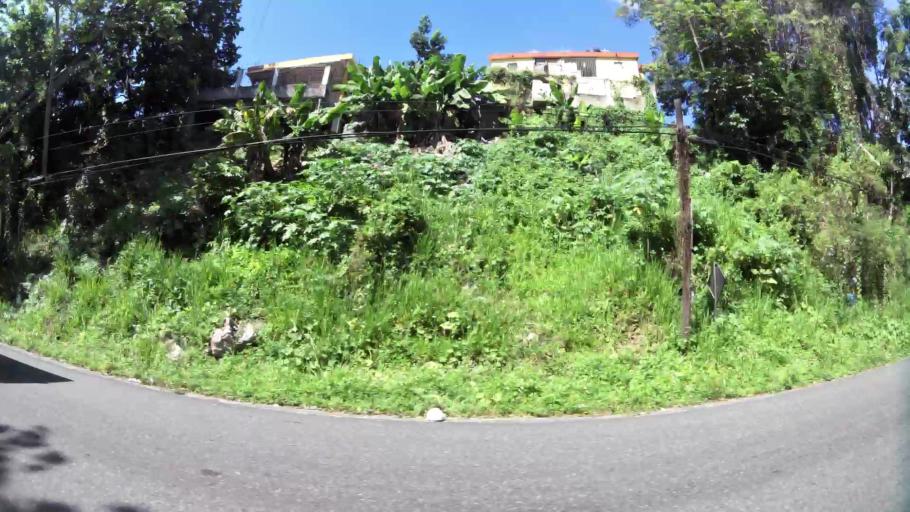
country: DO
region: San Cristobal
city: San Cristobal
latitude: 18.4293
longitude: -70.0870
